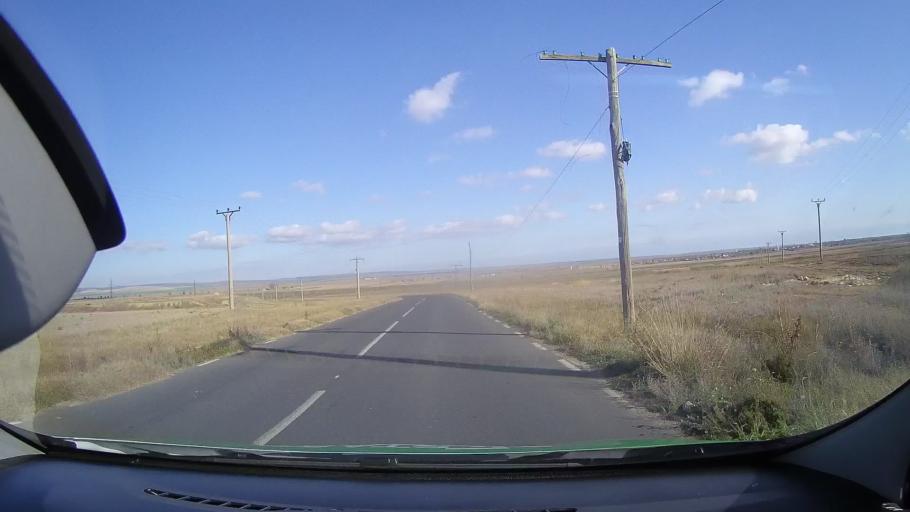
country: RO
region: Tulcea
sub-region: Comuna Ceamurlia de Jos
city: Ceamurlia de Jos
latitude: 44.7423
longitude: 28.6966
